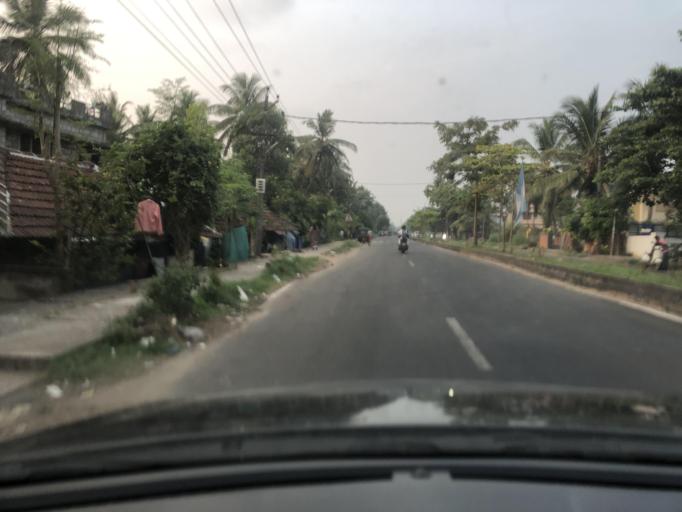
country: IN
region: Kerala
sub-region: Kozhikode
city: Kozhikode
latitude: 11.2924
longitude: 75.7580
